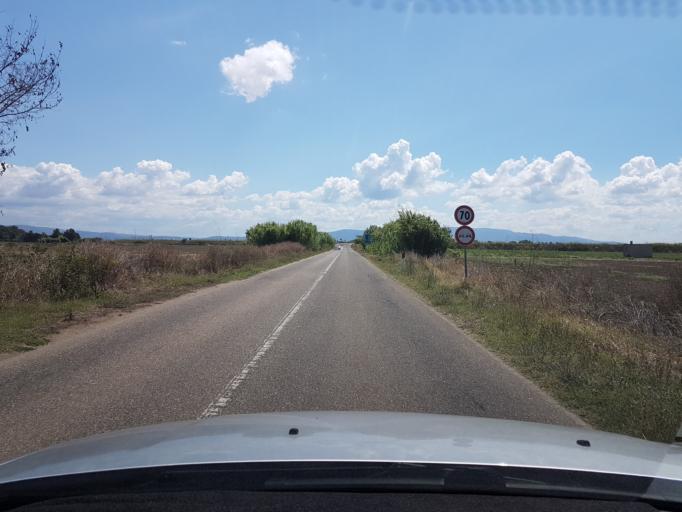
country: IT
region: Sardinia
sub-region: Provincia di Oristano
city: Solanas
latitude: 39.9193
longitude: 8.5503
